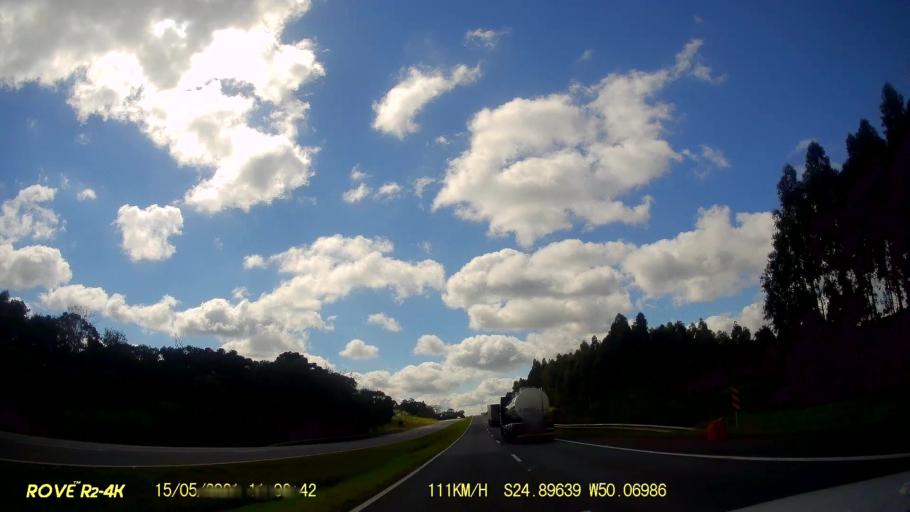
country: BR
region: Parana
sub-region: Carambei
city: Carambei
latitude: -24.8967
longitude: -50.0702
